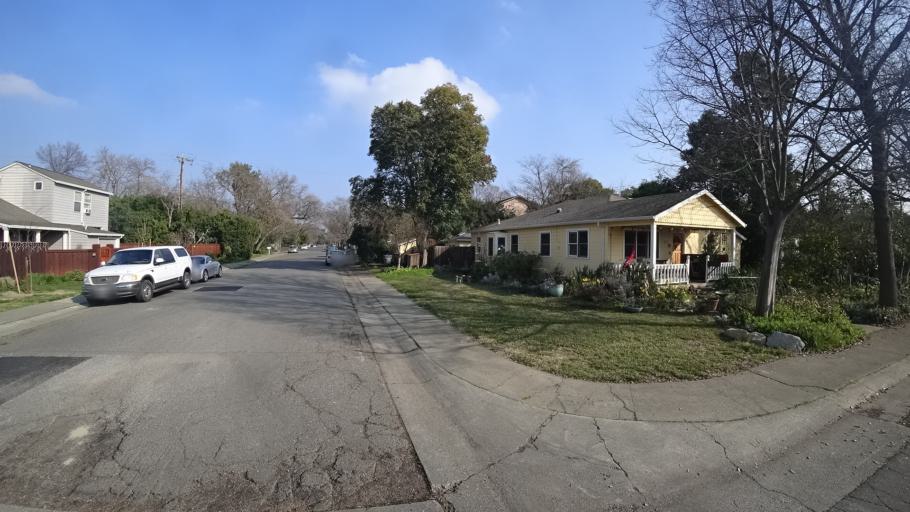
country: US
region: California
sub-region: Yolo County
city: Davis
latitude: 38.5530
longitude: -121.7443
